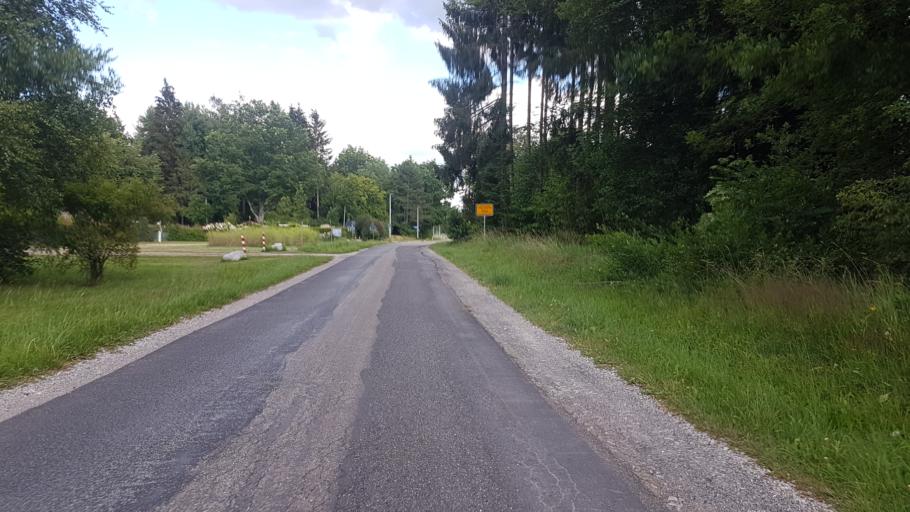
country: DE
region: Baden-Wuerttemberg
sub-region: Freiburg Region
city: Monchweiler
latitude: 48.0617
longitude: 8.4233
